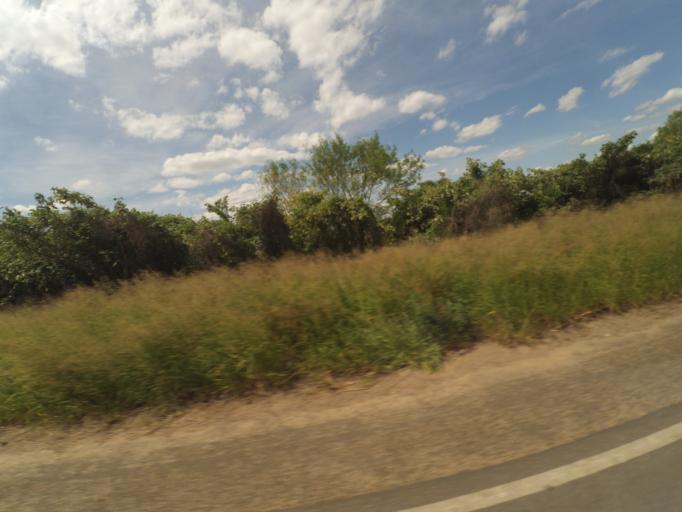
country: BO
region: Santa Cruz
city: Pailon
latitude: -17.5855
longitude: -62.0522
